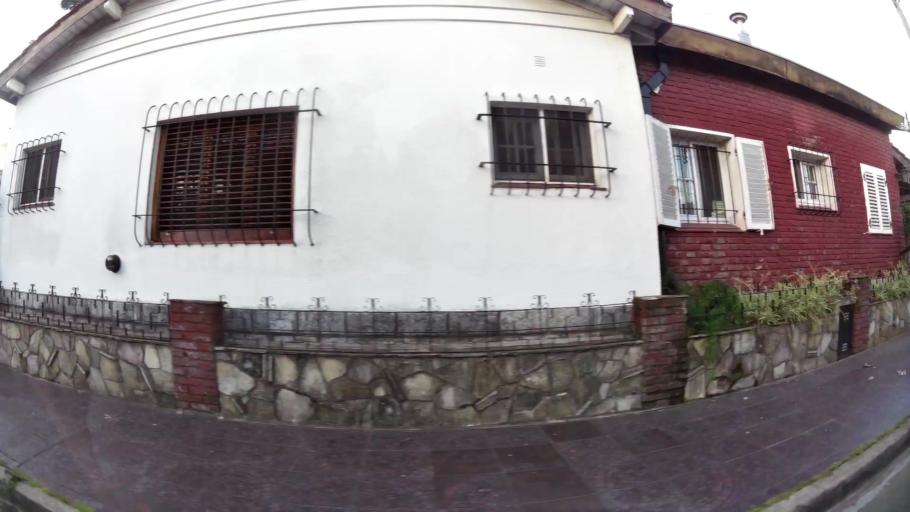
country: AR
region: Buenos Aires
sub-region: Partido de Moron
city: Moron
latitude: -34.6495
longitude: -58.6387
